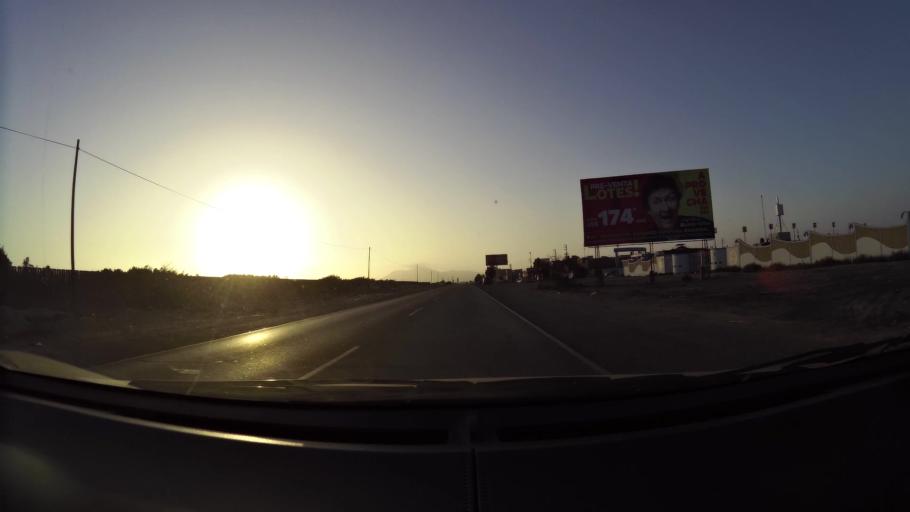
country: PE
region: Ancash
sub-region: Provincia de Santa
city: Buenos Aires
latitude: -9.1389
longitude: -78.5199
